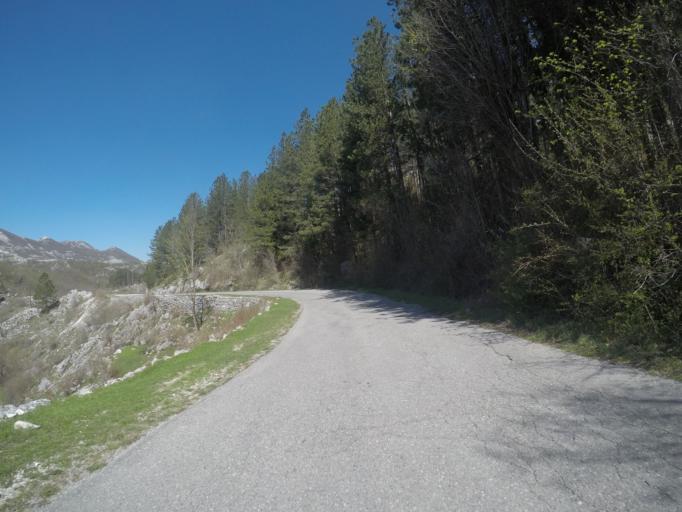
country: ME
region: Cetinje
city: Cetinje
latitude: 42.4656
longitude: 18.8604
